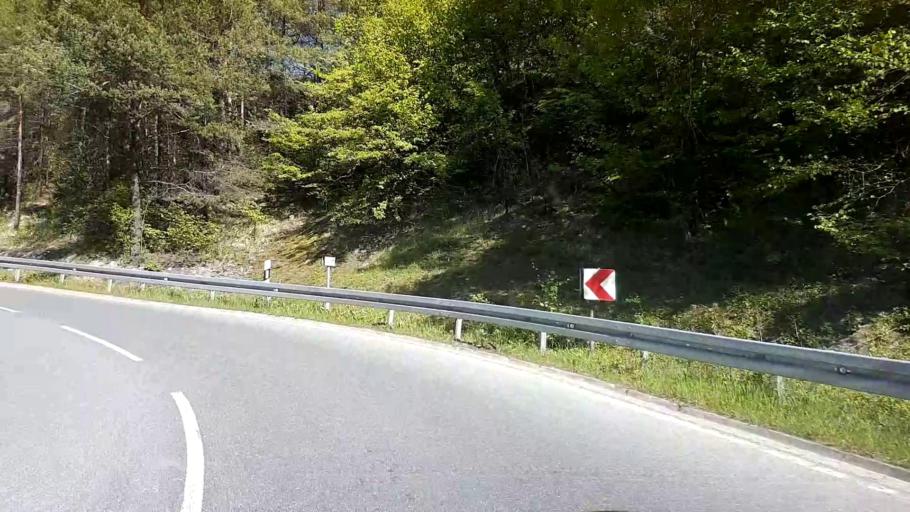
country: DE
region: Bavaria
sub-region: Upper Franconia
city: Weilersbach
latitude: 49.8070
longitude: 11.1274
